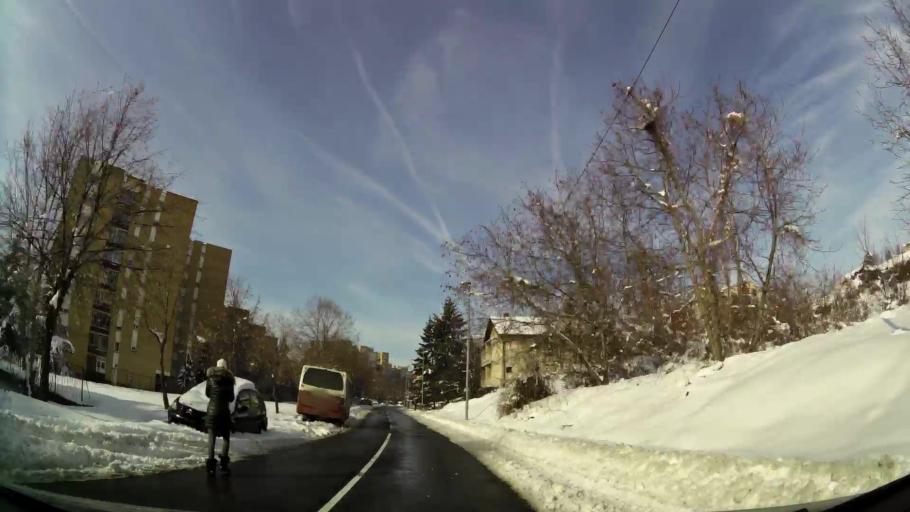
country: RS
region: Central Serbia
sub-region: Belgrade
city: Zvezdara
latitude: 44.7907
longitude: 20.5370
